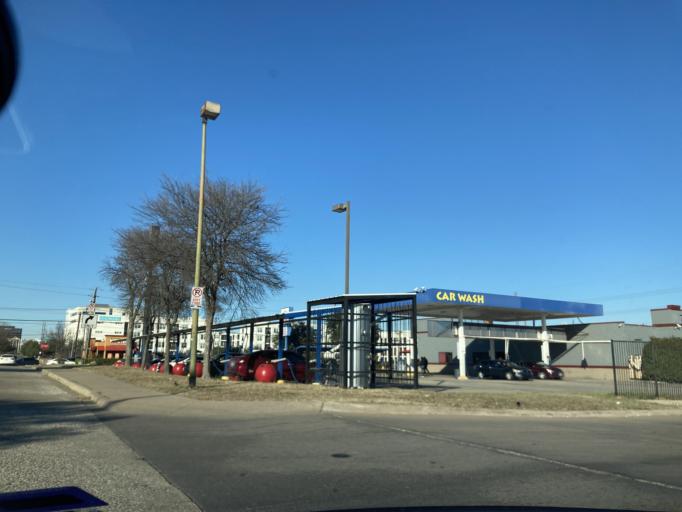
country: US
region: Texas
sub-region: Dallas County
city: Richardson
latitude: 32.9081
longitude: -96.7670
